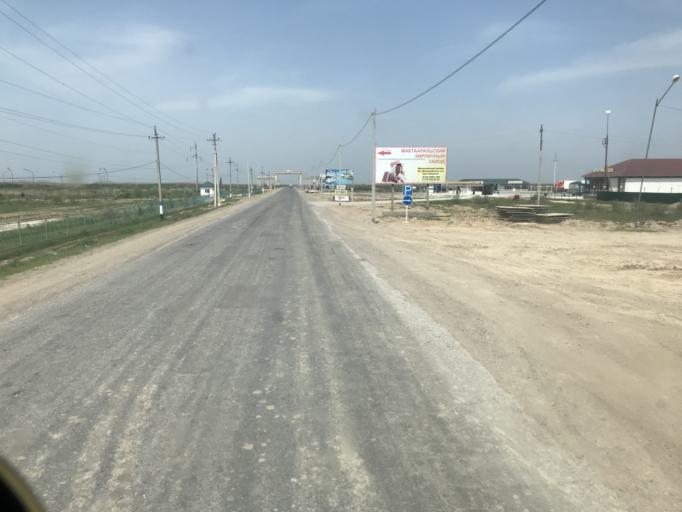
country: KZ
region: Ongtustik Qazaqstan
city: Asykata
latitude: 40.9610
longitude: 68.4612
